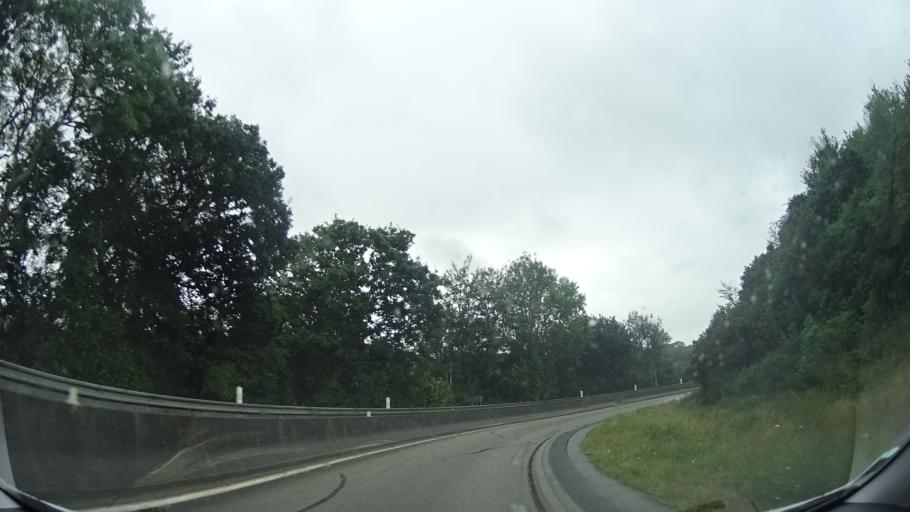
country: FR
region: Lower Normandy
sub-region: Departement de la Manche
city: Beaumont-Hague
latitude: 49.6144
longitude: -1.7878
